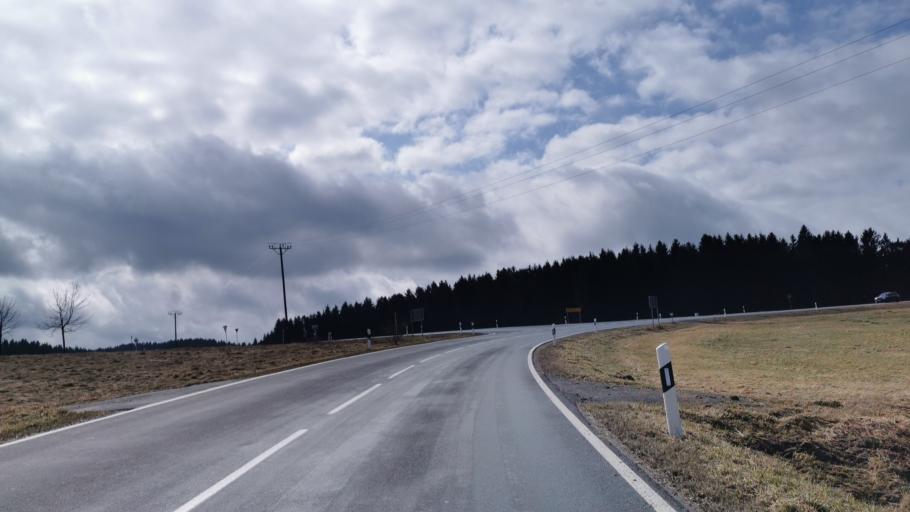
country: DE
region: Bavaria
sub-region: Upper Franconia
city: Reichenbach
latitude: 50.4217
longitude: 11.4051
